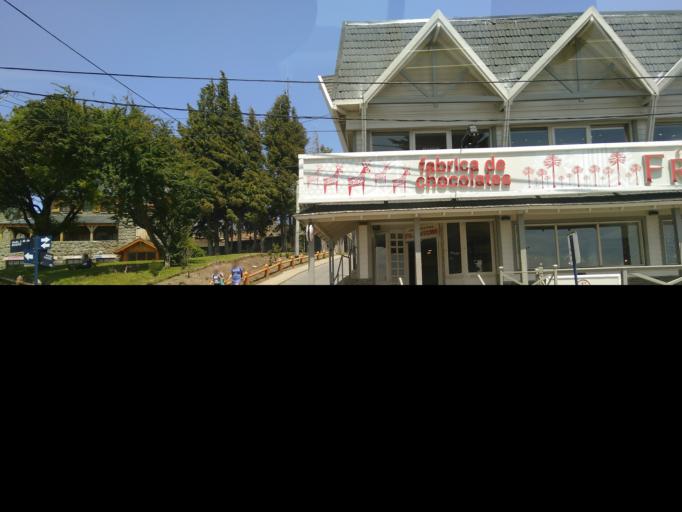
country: AR
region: Rio Negro
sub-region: Departamento de Bariloche
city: San Carlos de Bariloche
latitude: -41.1327
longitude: -71.3111
